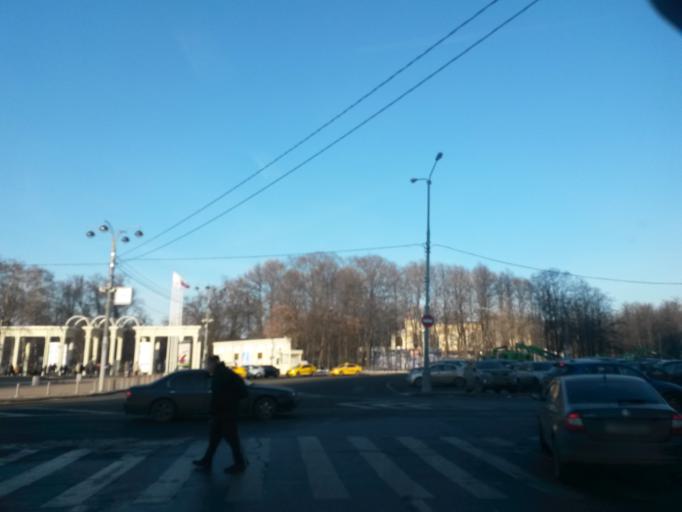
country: RU
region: Moscow
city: Sokol'niki
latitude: 55.7921
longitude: 37.6786
